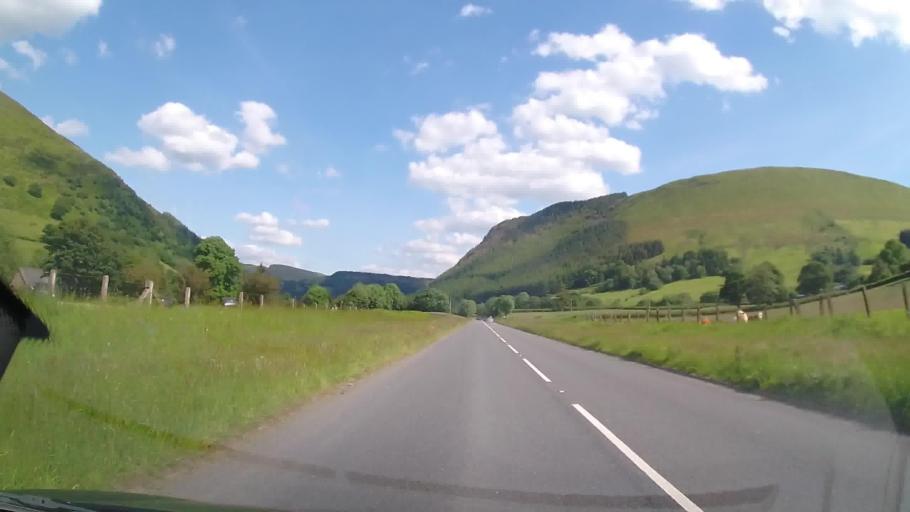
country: GB
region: Wales
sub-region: Gwynedd
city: Corris
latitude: 52.7293
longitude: -3.7147
